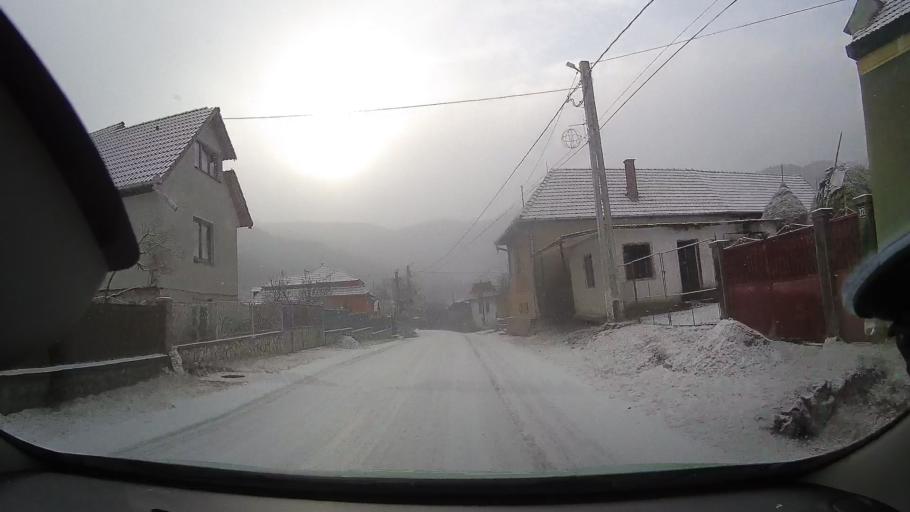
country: RO
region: Alba
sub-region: Comuna Rimetea
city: Rimetea
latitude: 46.3889
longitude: 23.5621
